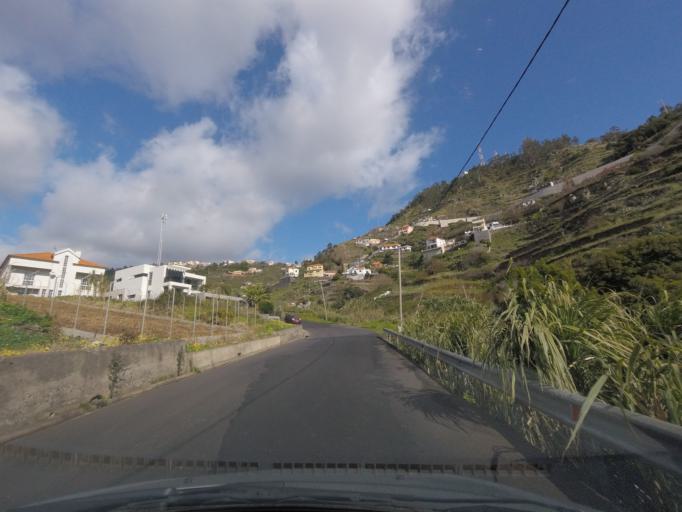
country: PT
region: Madeira
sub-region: Ribeira Brava
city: Campanario
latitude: 32.6601
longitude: -17.0106
